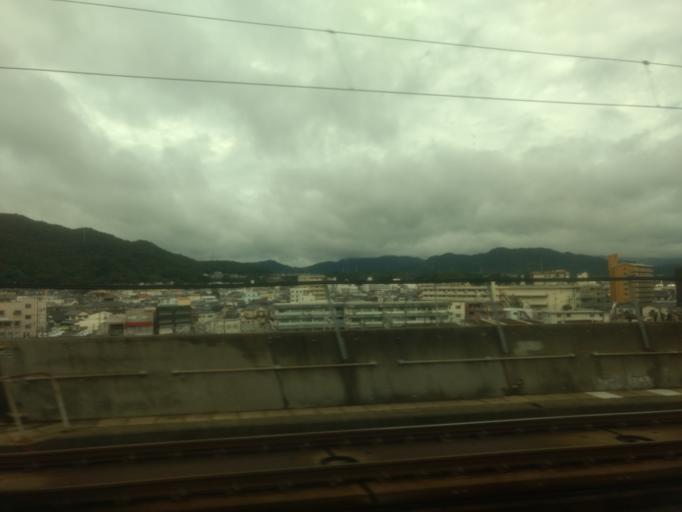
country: JP
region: Yamaguchi
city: Ogori-shimogo
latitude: 34.0943
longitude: 131.3992
